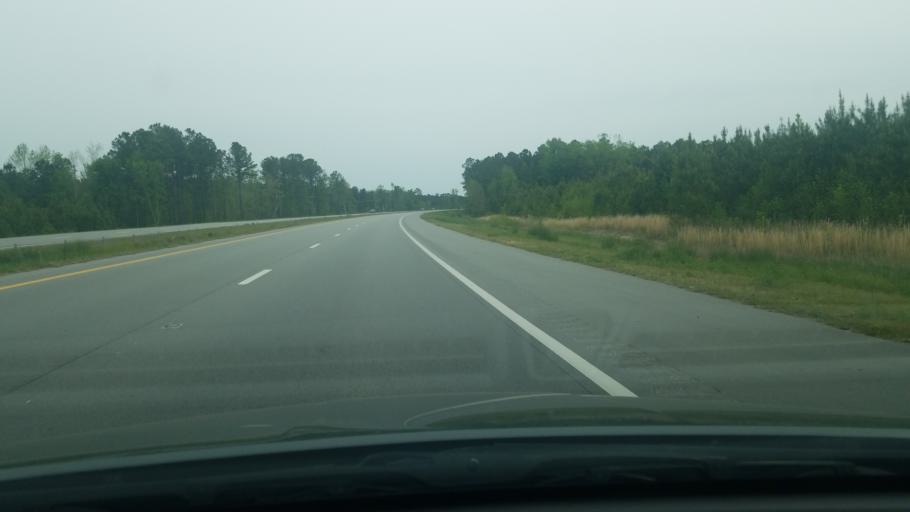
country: US
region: North Carolina
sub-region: Craven County
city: River Bend
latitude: 35.0341
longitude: -77.2246
